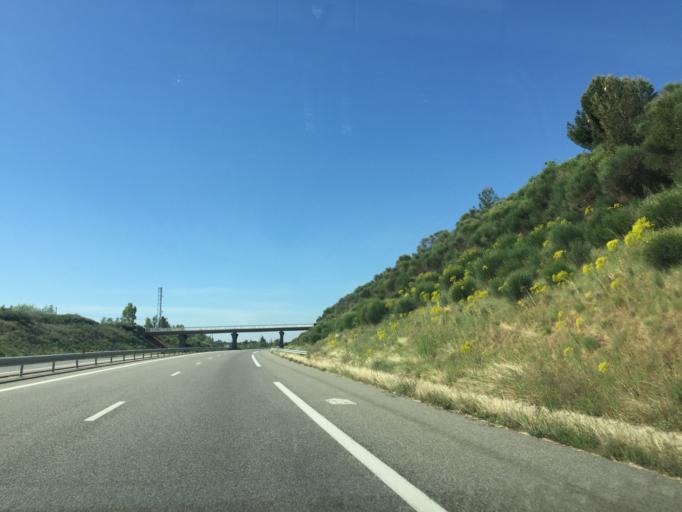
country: FR
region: Provence-Alpes-Cote d'Azur
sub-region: Departement des Alpes-de-Haute-Provence
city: Volonne
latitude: 44.0941
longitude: 5.9925
